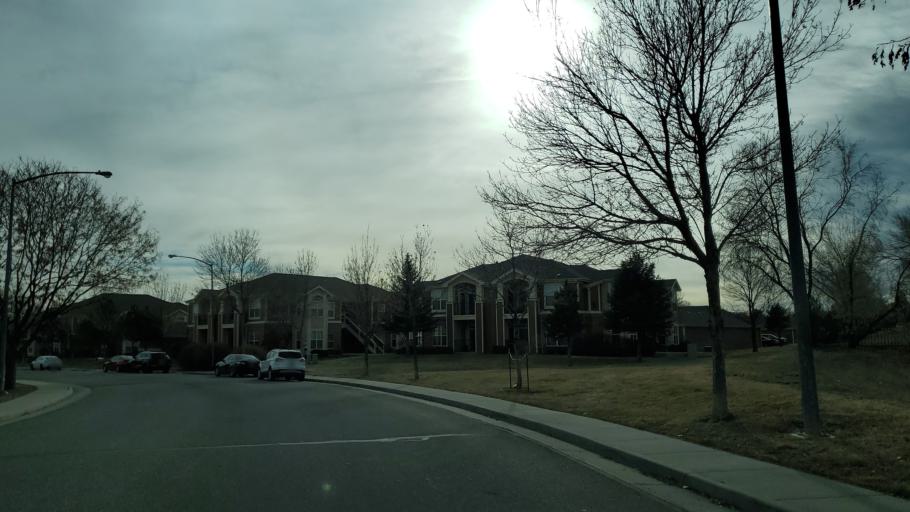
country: US
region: Colorado
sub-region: Adams County
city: Northglenn
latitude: 39.9165
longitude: -104.9498
